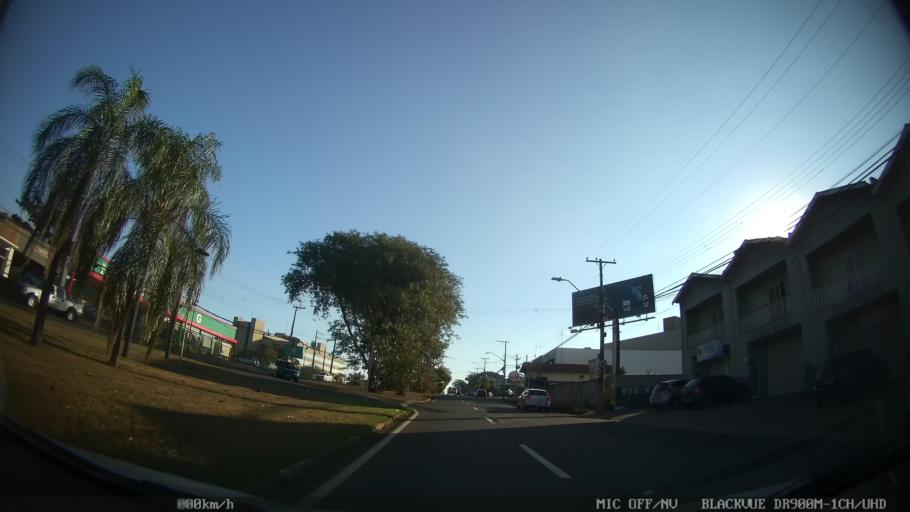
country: BR
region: Sao Paulo
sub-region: Piracicaba
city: Piracicaba
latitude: -22.7033
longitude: -47.6523
